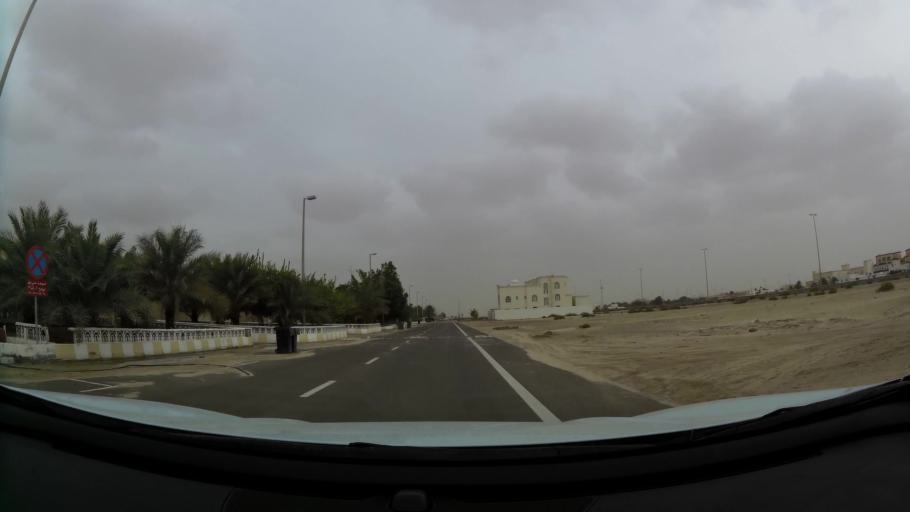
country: AE
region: Abu Dhabi
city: Abu Dhabi
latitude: 24.3698
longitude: 54.6619
